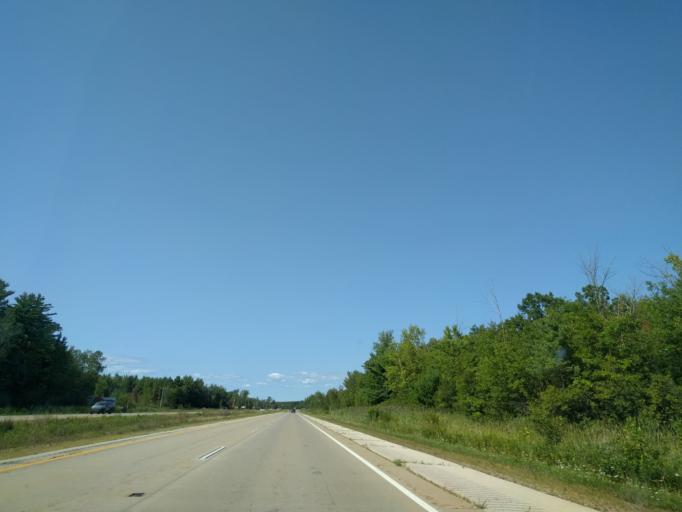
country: US
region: Wisconsin
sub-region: Oconto County
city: Oconto
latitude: 44.8582
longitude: -87.8991
